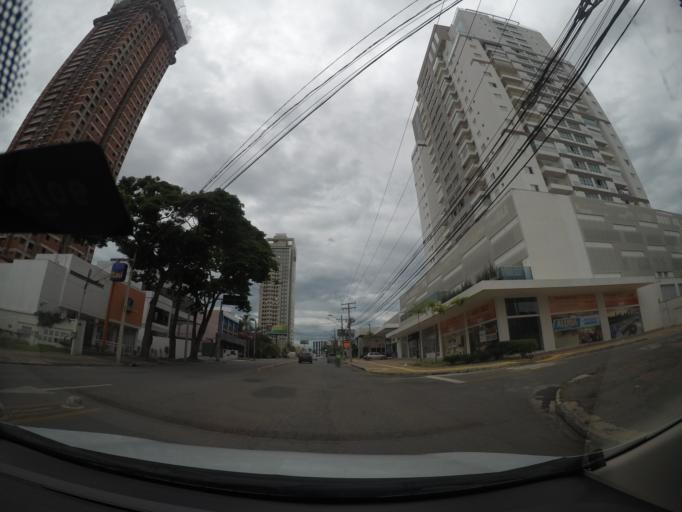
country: BR
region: Goias
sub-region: Goiania
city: Goiania
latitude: -16.7050
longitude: -49.2675
